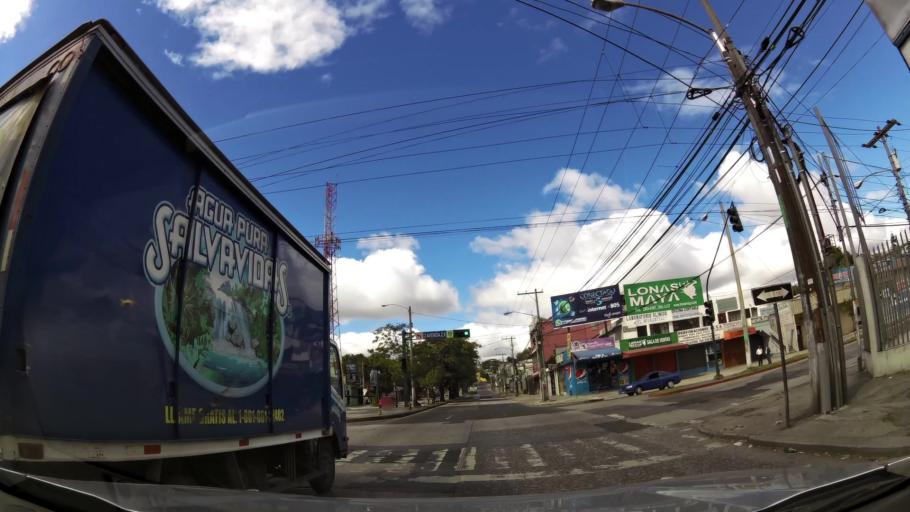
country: GT
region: Guatemala
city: Guatemala City
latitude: 14.6108
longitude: -90.5231
